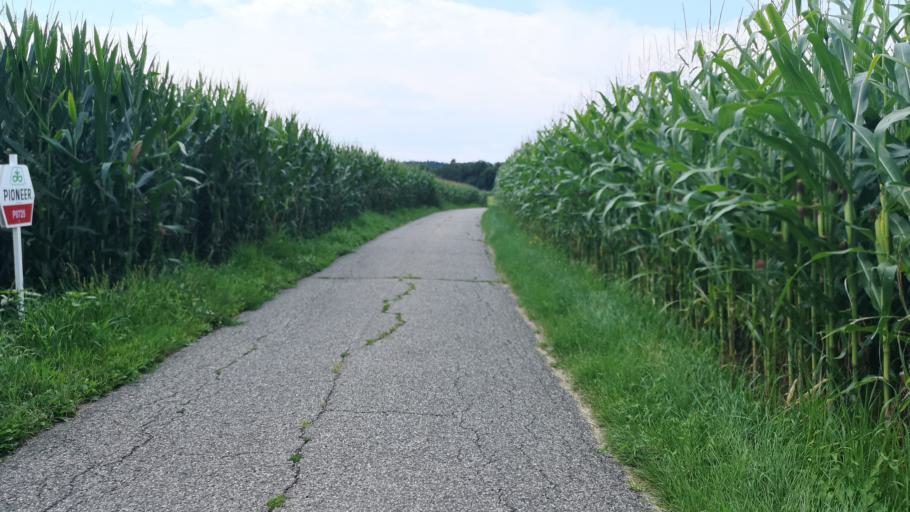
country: AT
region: Styria
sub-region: Politischer Bezirk Leibnitz
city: Weitendorf
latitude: 46.8897
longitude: 15.4756
